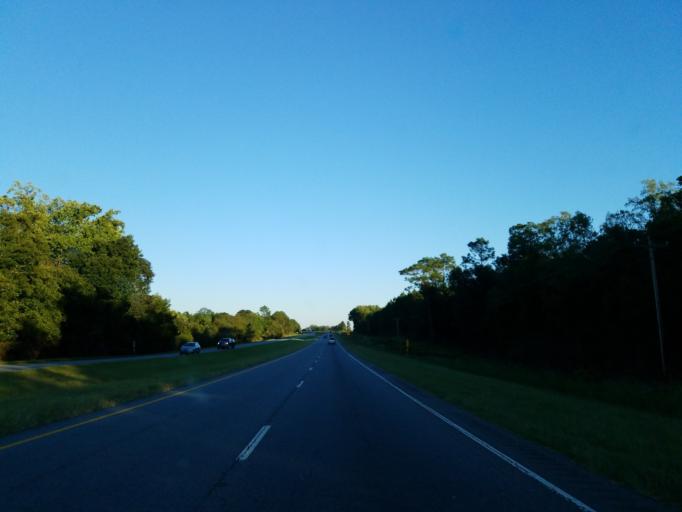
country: US
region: Georgia
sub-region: Worth County
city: Sylvester
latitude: 31.4864
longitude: -83.7004
